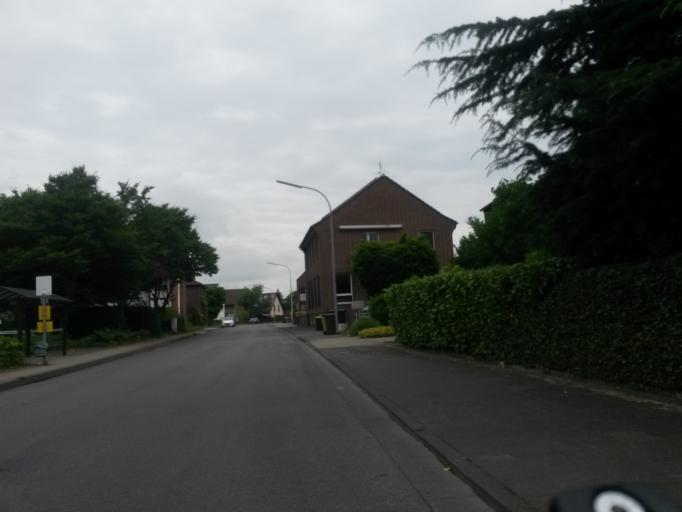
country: DE
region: North Rhine-Westphalia
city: Kempen
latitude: 51.3778
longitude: 6.4466
